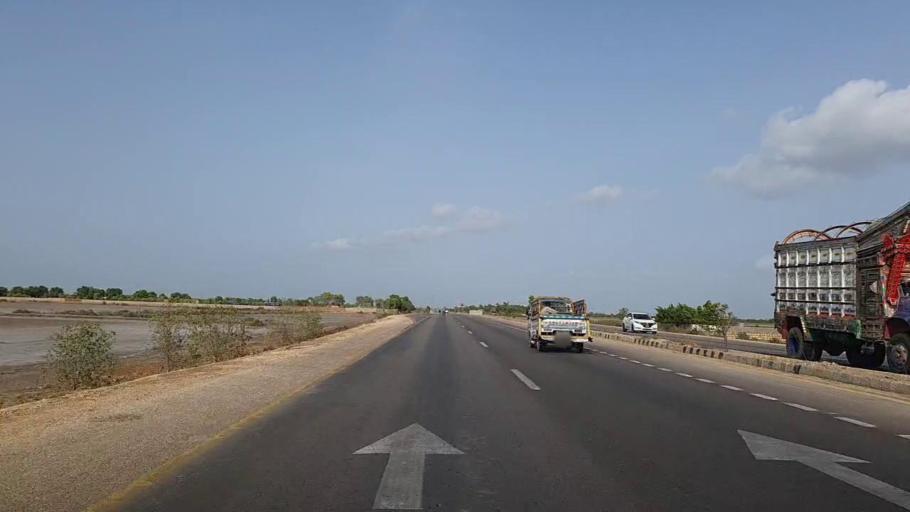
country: PK
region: Sindh
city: Gharo
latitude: 24.7383
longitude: 67.7294
